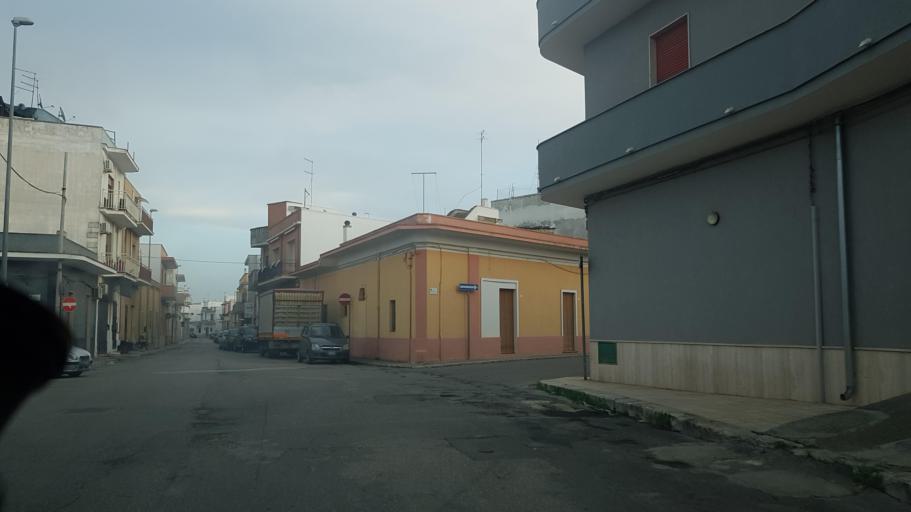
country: IT
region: Apulia
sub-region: Provincia di Brindisi
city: San Pancrazio Salentino
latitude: 40.4193
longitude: 17.8333
